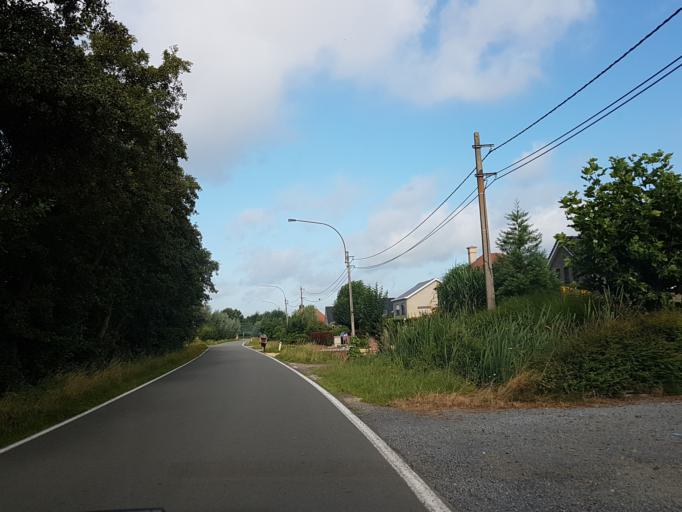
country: BE
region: Flanders
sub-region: Provincie Oost-Vlaanderen
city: Lovendegem
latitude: 51.0659
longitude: 3.6202
